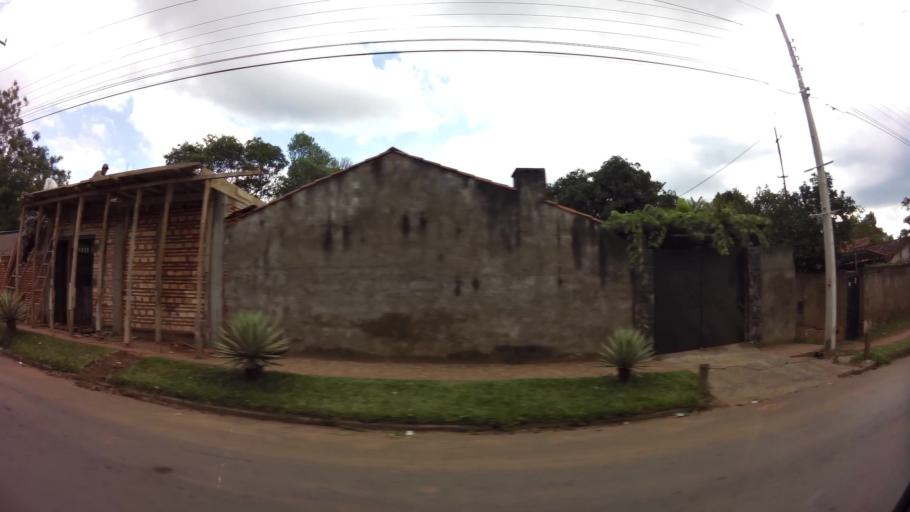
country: PY
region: Central
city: San Lorenzo
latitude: -25.2888
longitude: -57.5017
